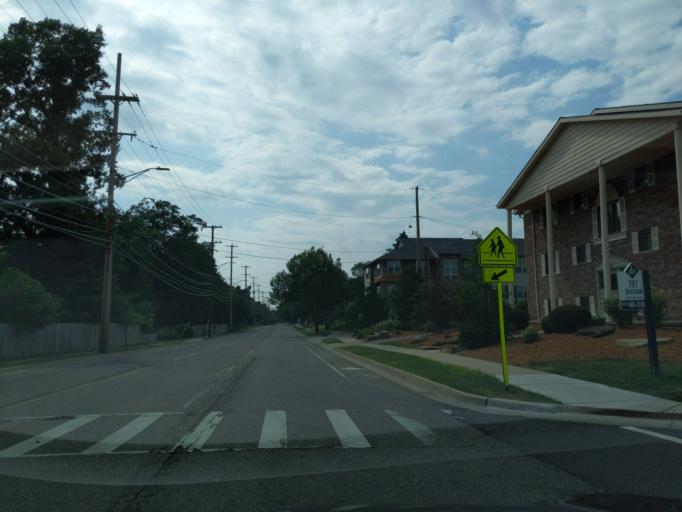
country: US
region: Michigan
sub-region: Ingham County
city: East Lansing
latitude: 42.7407
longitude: -84.4720
